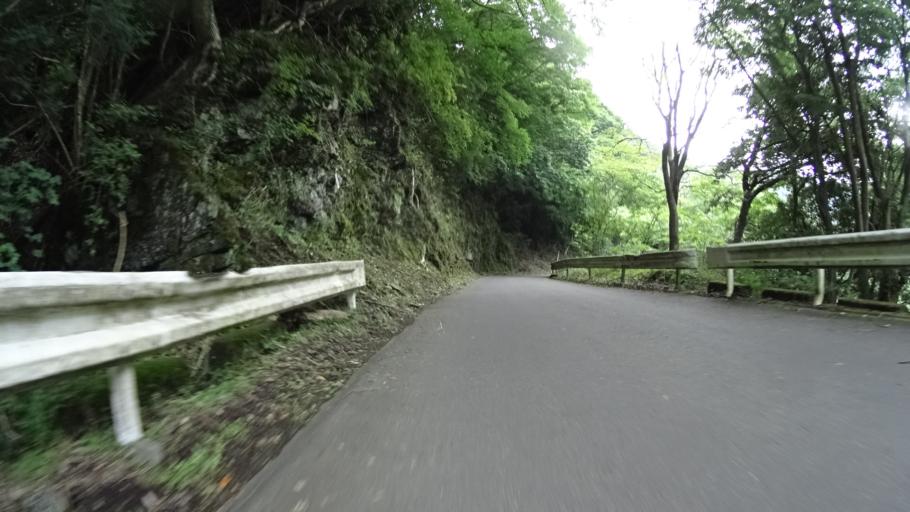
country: JP
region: Kanagawa
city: Hadano
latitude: 35.4904
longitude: 139.2200
